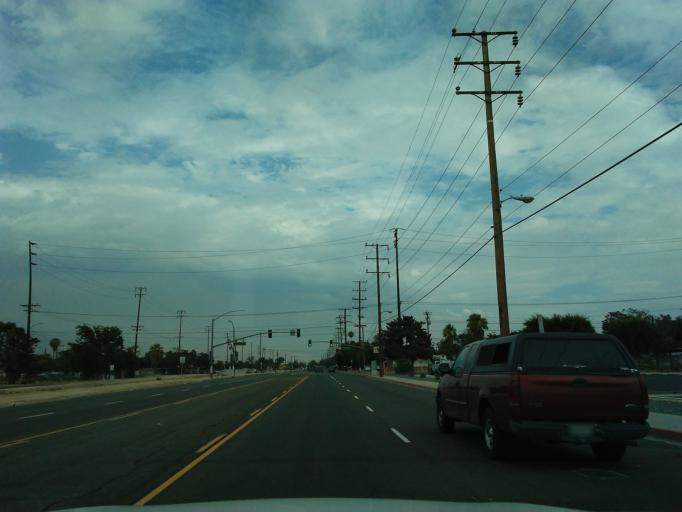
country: US
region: California
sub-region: San Bernardino County
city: San Bernardino
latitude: 34.1043
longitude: -117.2690
